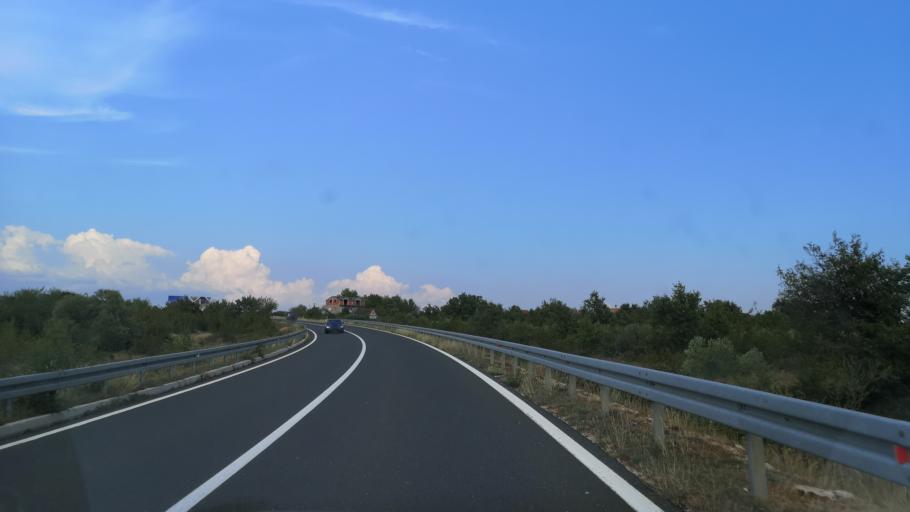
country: HR
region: Sibensko-Kniniska
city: Zaton
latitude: 43.8839
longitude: 15.7743
